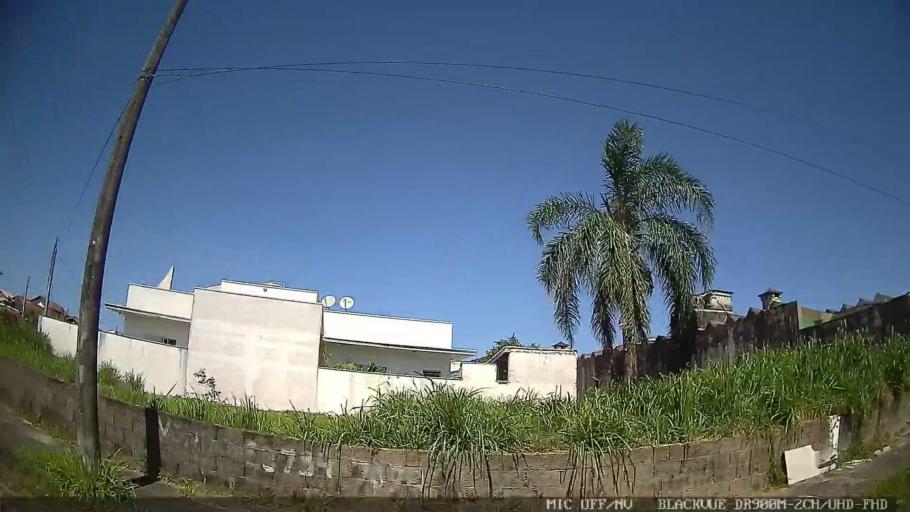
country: BR
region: Sao Paulo
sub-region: Peruibe
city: Peruibe
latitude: -24.2938
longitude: -46.9736
